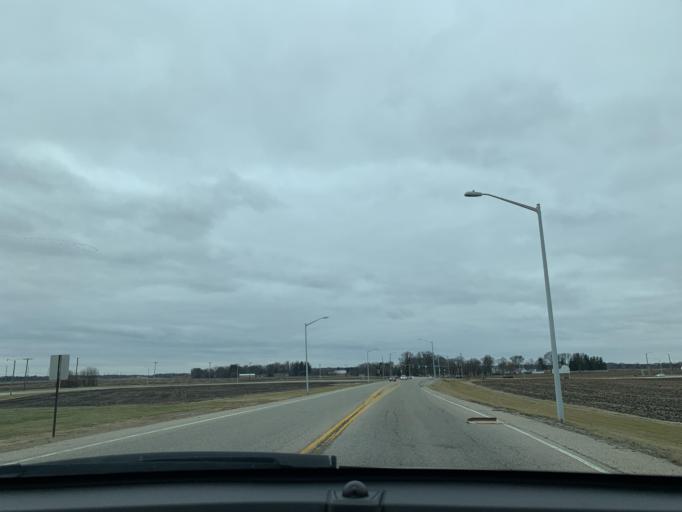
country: US
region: Illinois
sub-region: Sangamon County
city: Jerome
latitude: 39.7402
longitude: -89.6882
